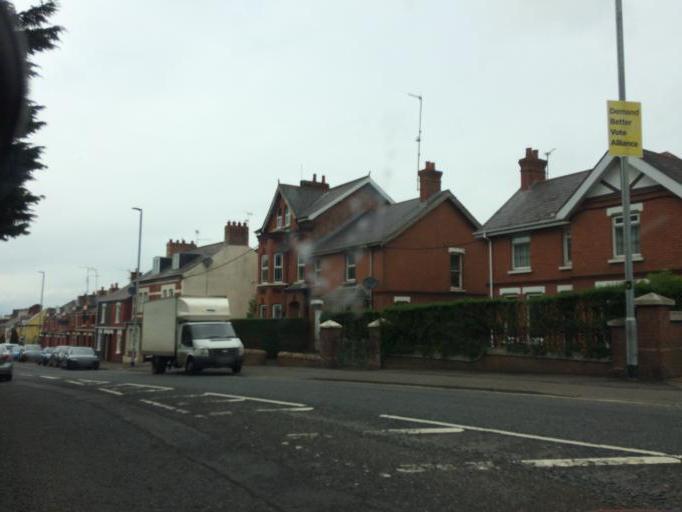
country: GB
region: Northern Ireland
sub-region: Antrim Borough
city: Antrim
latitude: 54.7134
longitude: -6.2096
